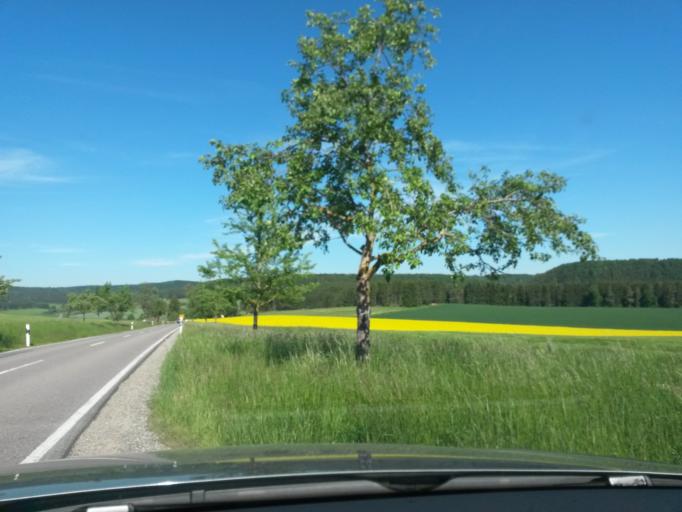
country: DE
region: Baden-Wuerttemberg
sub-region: Tuebingen Region
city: Langenenslingen
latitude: 48.1804
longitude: 9.3842
